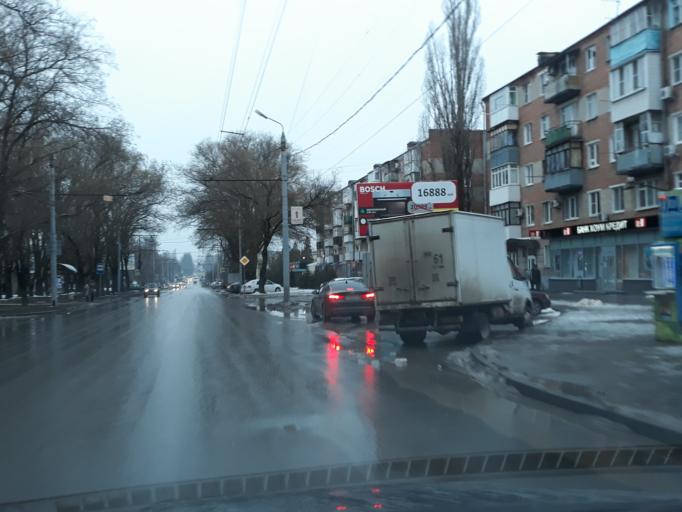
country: RU
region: Rostov
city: Taganrog
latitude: 47.2554
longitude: 38.9179
